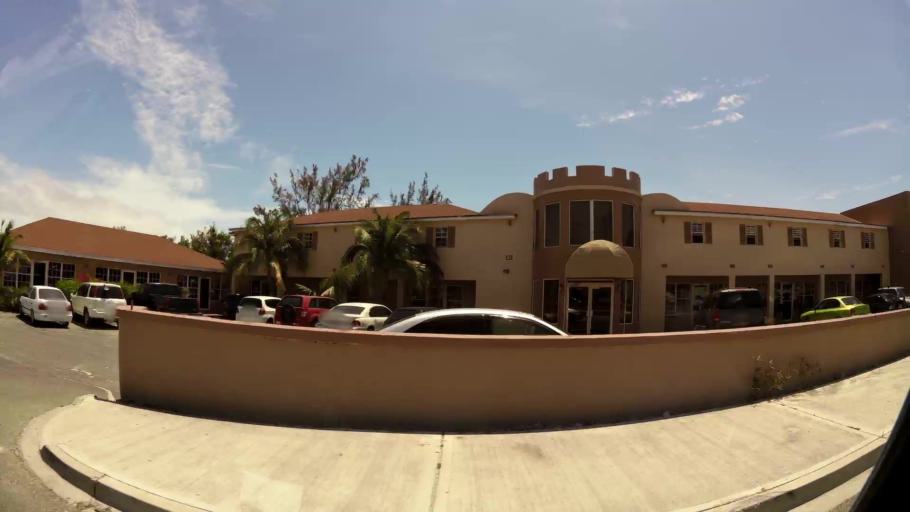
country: BS
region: Mayaguana
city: Abraham's Bay
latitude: 21.7764
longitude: -72.2651
